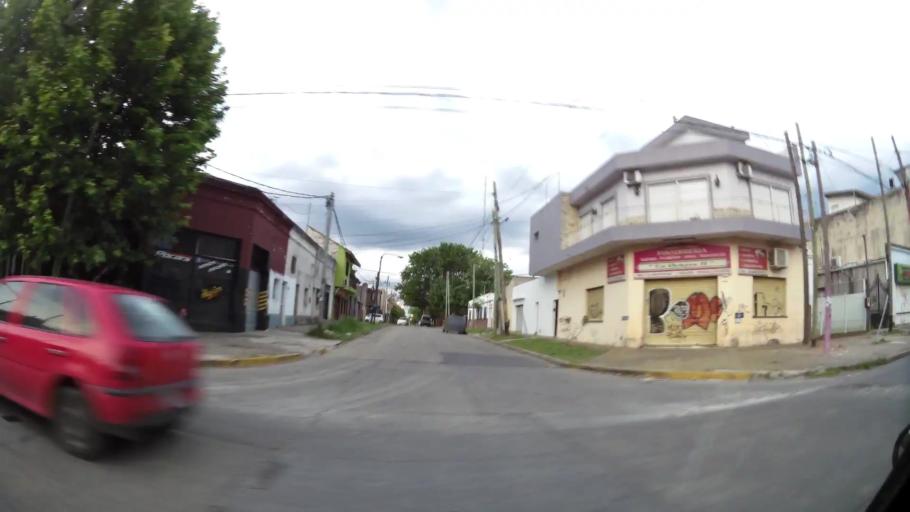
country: AR
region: Buenos Aires
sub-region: Partido de Quilmes
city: Quilmes
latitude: -34.7361
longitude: -58.2415
